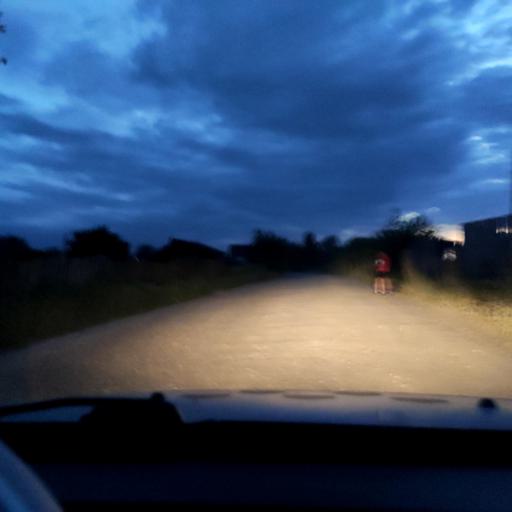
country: RU
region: Perm
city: Kondratovo
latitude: 58.0291
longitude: 56.0670
